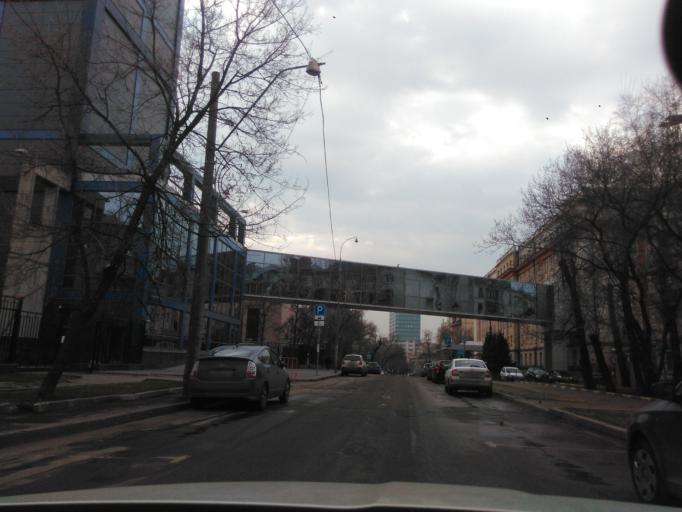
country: RU
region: Moskovskaya
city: Dorogomilovo
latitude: 55.7885
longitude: 37.5775
